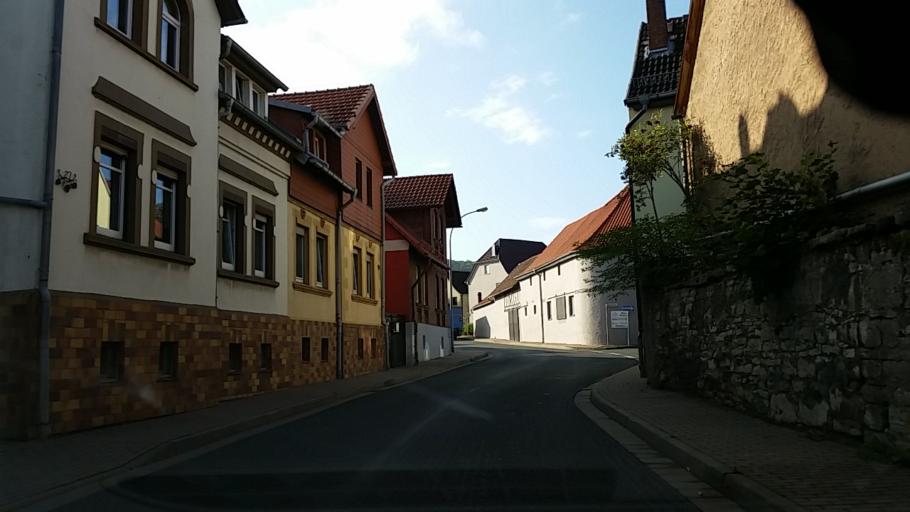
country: DE
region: Thuringia
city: Kleinfurra
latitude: 51.3947
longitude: 10.7986
